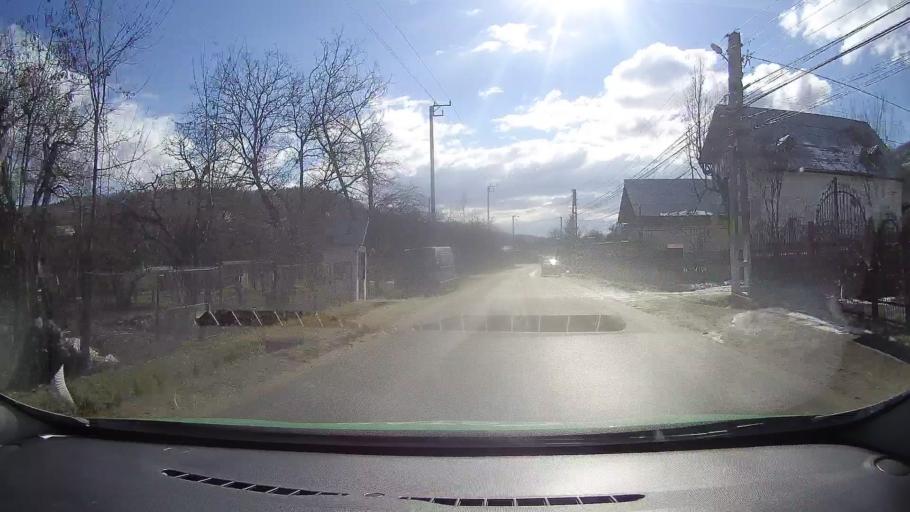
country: RO
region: Dambovita
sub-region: Comuna Runcu
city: Runcu
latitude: 45.1730
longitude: 25.3918
